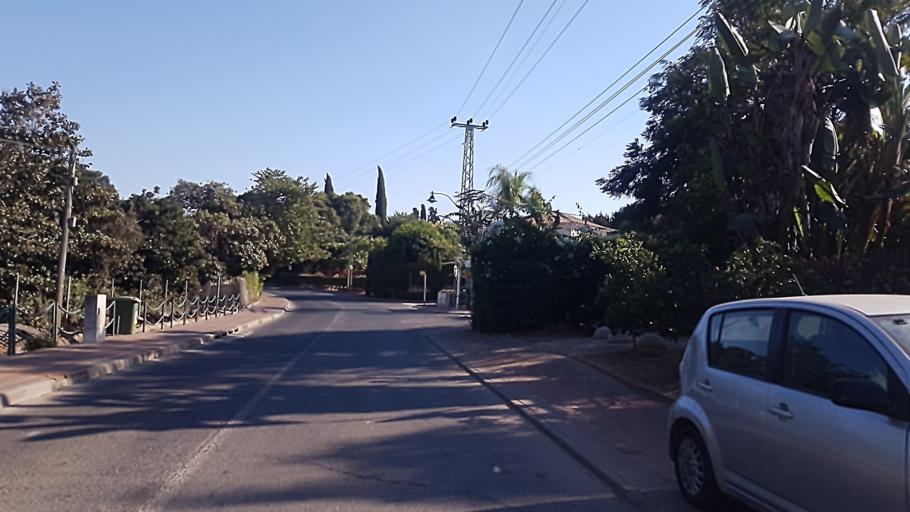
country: IL
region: Central District
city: Kfar Saba
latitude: 32.2052
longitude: 34.9052
